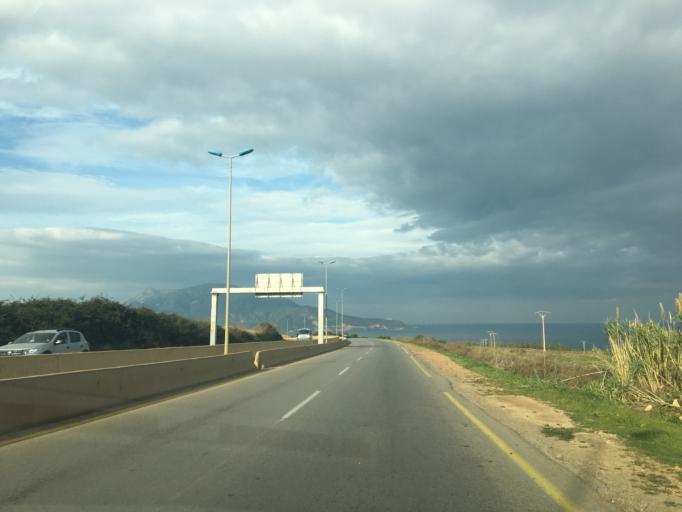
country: DZ
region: Tipaza
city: Tipasa
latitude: 36.5803
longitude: 2.4913
